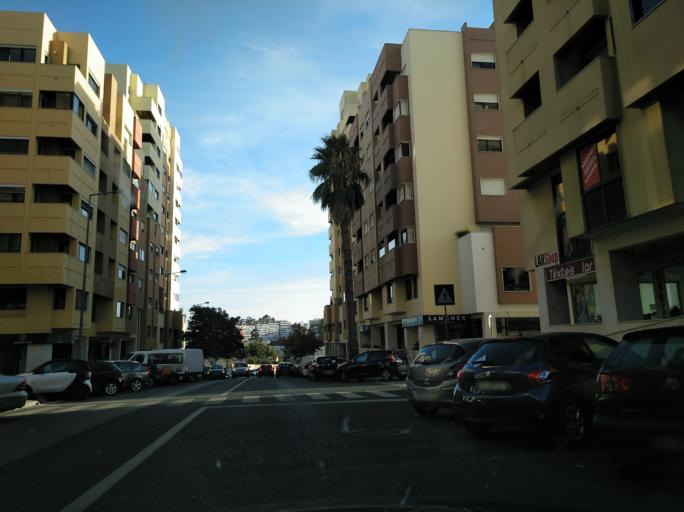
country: PT
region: Lisbon
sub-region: Odivelas
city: Pontinha
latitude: 38.7610
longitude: -9.1797
